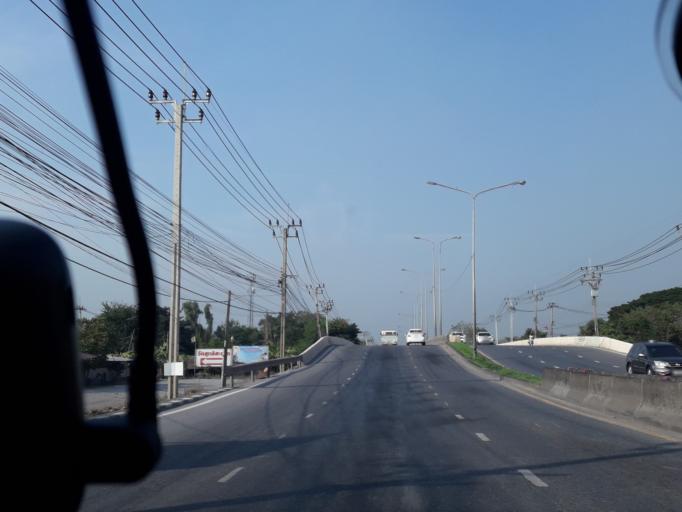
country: TH
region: Bangkok
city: Khlong Sam Wa
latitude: 13.8791
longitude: 100.7317
